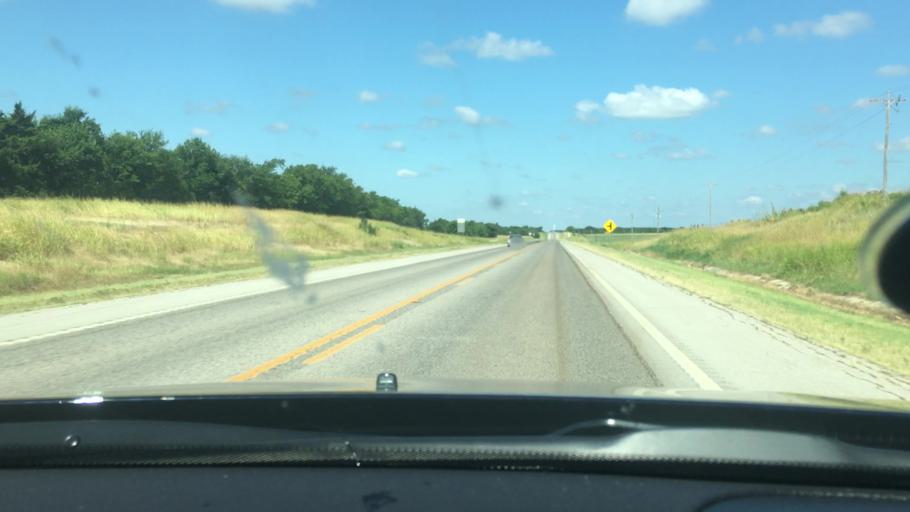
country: US
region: Oklahoma
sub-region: Marshall County
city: Oakland
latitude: 34.1000
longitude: -96.8842
